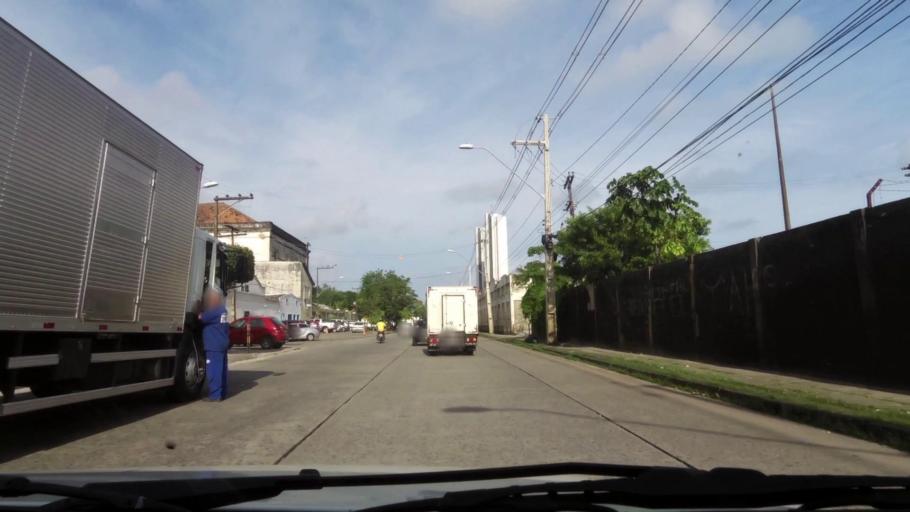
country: BR
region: Pernambuco
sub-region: Recife
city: Recife
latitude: -8.0721
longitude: -34.8798
